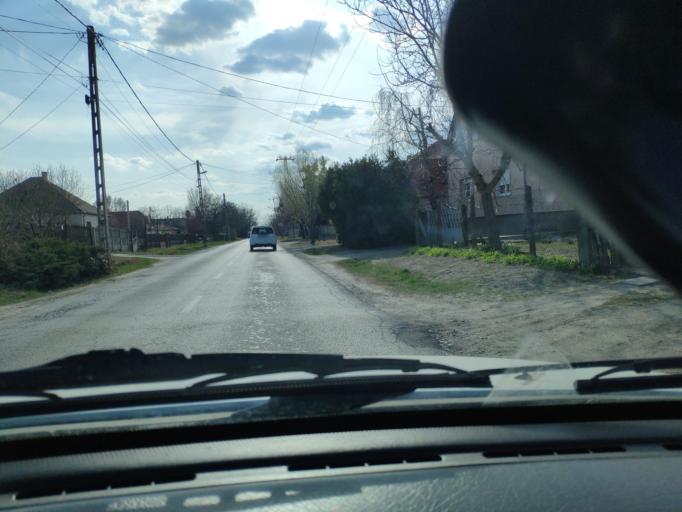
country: HU
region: Pest
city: Rackeve
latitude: 47.1554
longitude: 18.9268
